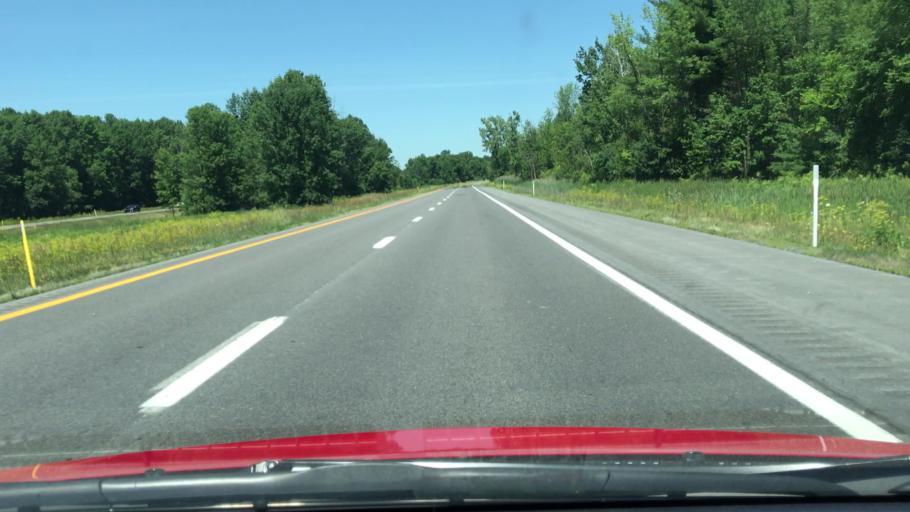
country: US
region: New York
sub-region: Clinton County
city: Champlain
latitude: 44.8482
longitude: -73.4477
